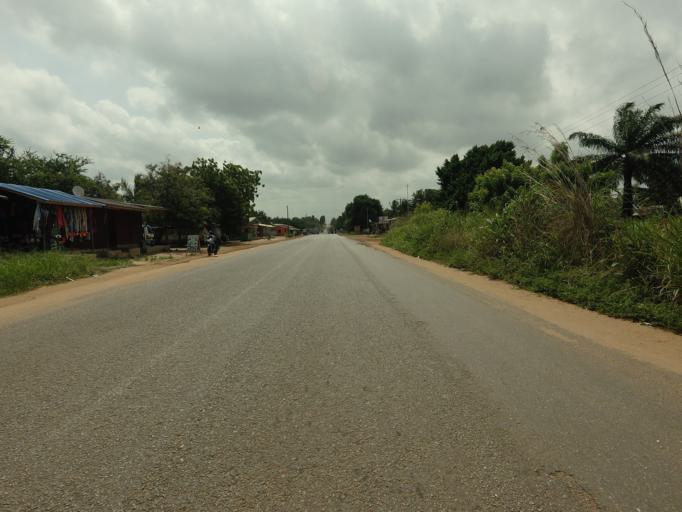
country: TG
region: Maritime
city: Lome
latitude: 6.1198
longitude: 1.1310
